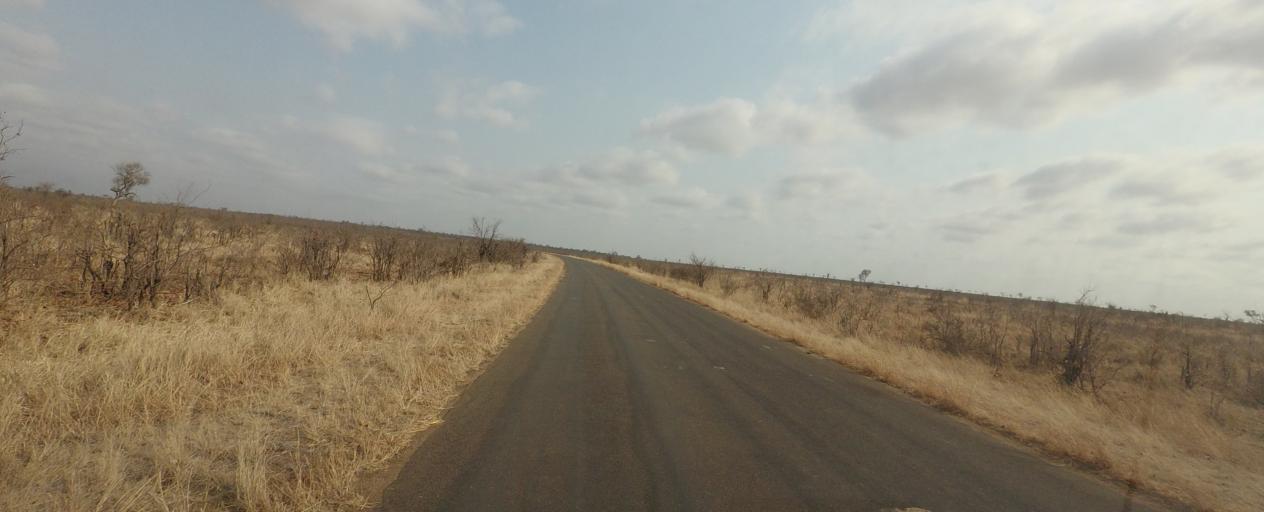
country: ZA
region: Limpopo
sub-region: Vhembe District Municipality
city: Mutale
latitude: -22.8999
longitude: 31.2527
